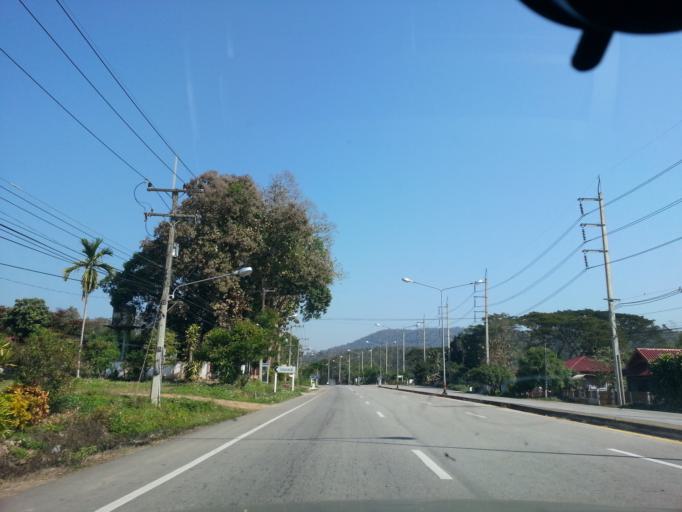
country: TH
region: Chiang Mai
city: Mae Taeng
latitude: 19.2172
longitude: 98.9713
